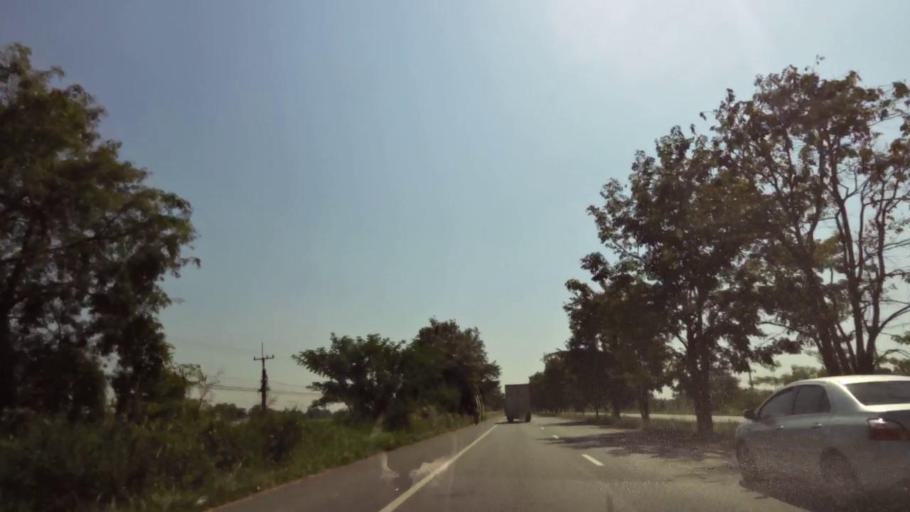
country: TH
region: Nakhon Sawan
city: Kao Liao
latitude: 15.9066
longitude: 100.1126
